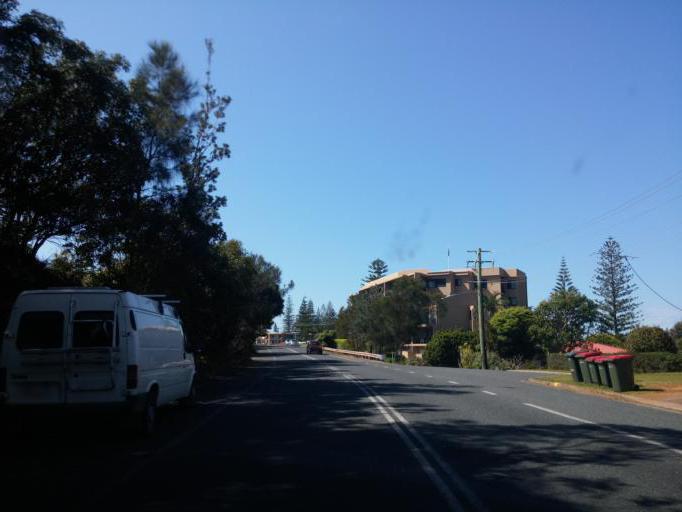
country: AU
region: New South Wales
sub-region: Port Macquarie-Hastings
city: Port Macquarie
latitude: -31.4462
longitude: 152.9284
